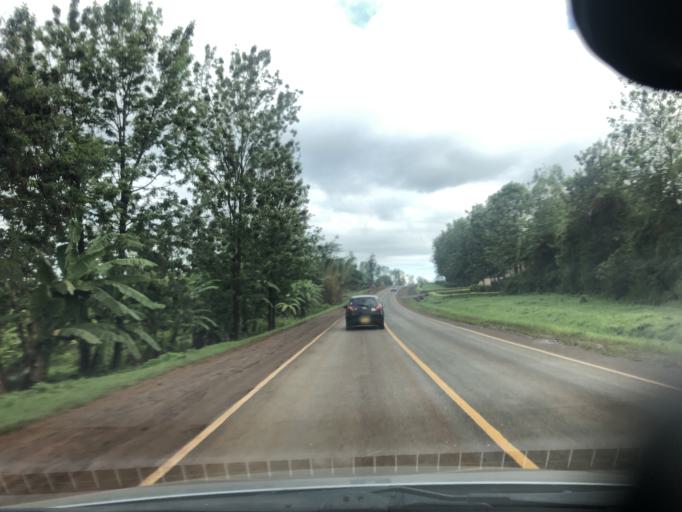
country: KE
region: Murang'a District
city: Maragua
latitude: -0.8303
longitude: 37.1375
